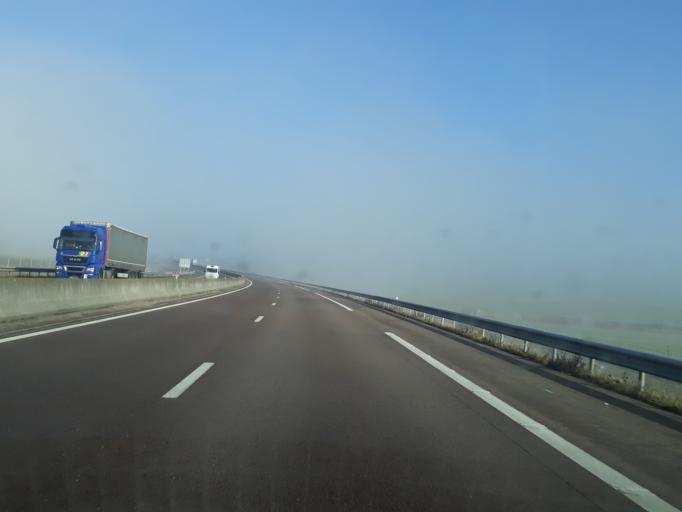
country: FR
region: Lorraine
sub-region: Departement des Vosges
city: Chatenois
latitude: 48.3570
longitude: 5.8651
